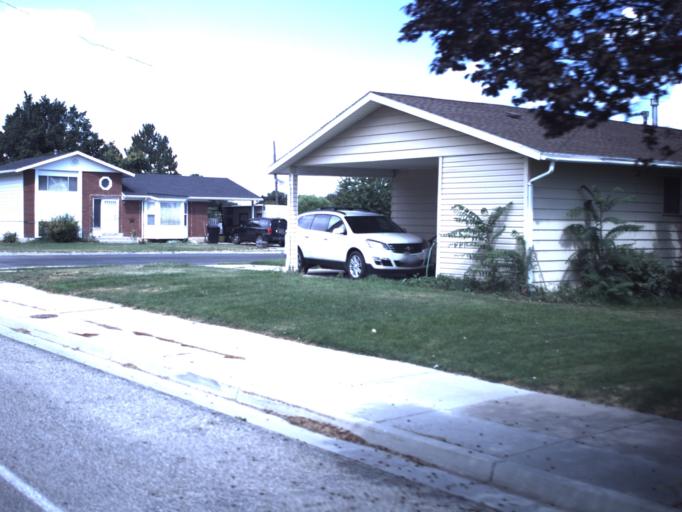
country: US
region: Utah
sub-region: Box Elder County
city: Garland
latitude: 41.7377
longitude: -112.1625
